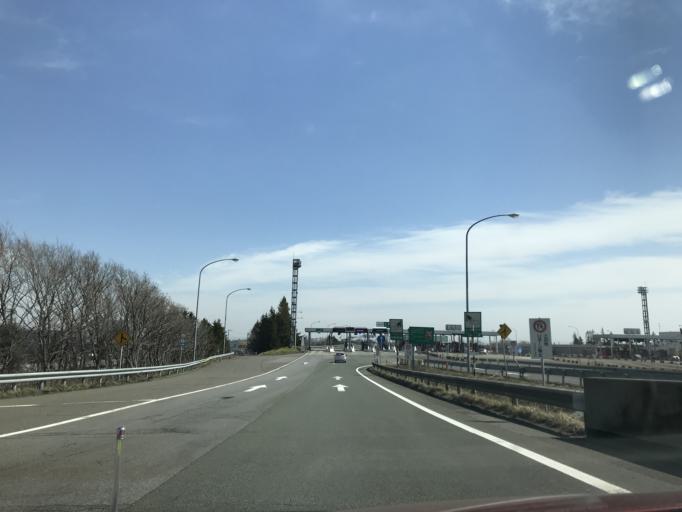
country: JP
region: Hokkaido
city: Sapporo
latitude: 43.0787
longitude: 141.4244
